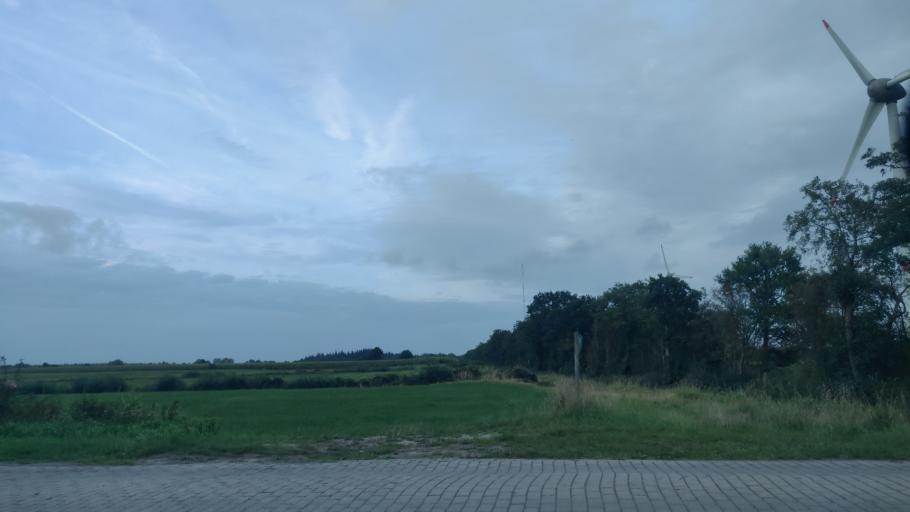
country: DE
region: Lower Saxony
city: Aurich
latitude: 53.5007
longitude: 7.4314
